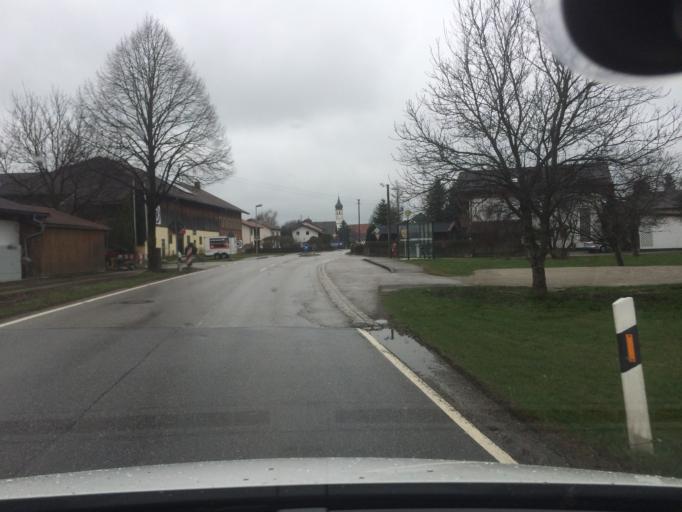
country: DE
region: Bavaria
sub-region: Upper Bavaria
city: Tuntenhausen
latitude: 47.9282
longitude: 11.9871
